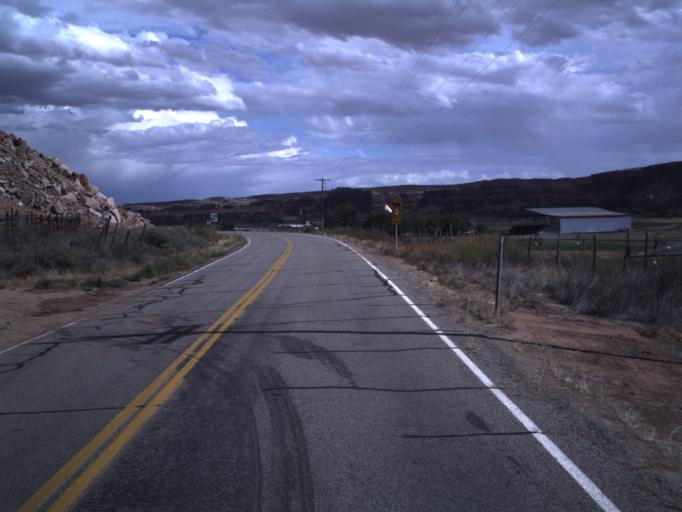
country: US
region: Utah
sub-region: San Juan County
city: Blanding
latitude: 37.2854
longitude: -109.5429
